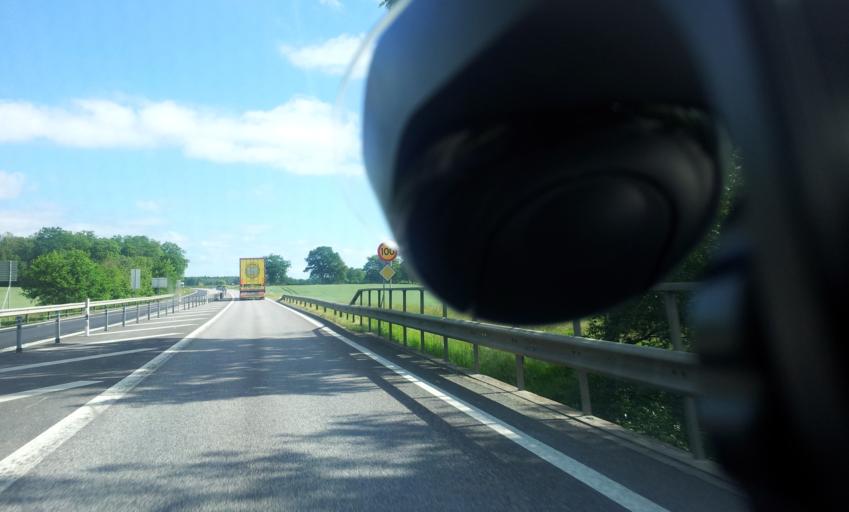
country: SE
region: Kalmar
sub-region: Kalmar Kommun
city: Lindsdal
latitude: 56.8032
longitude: 16.3631
